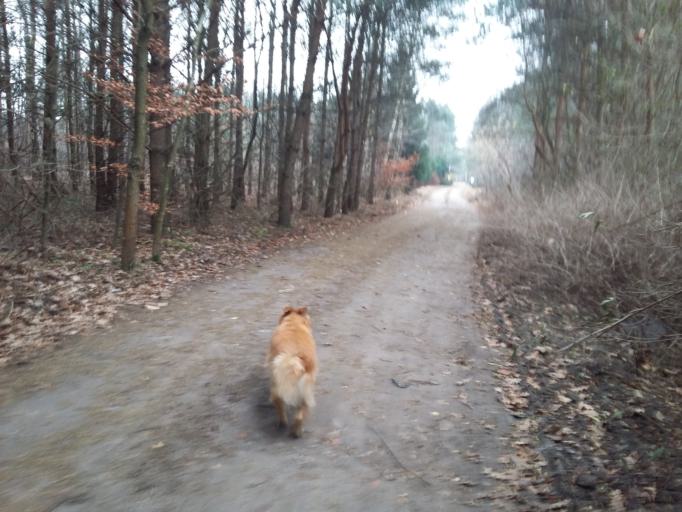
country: PL
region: Lodz Voivodeship
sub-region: Powiat pabianicki
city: Ksawerow
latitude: 51.7270
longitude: 19.3832
